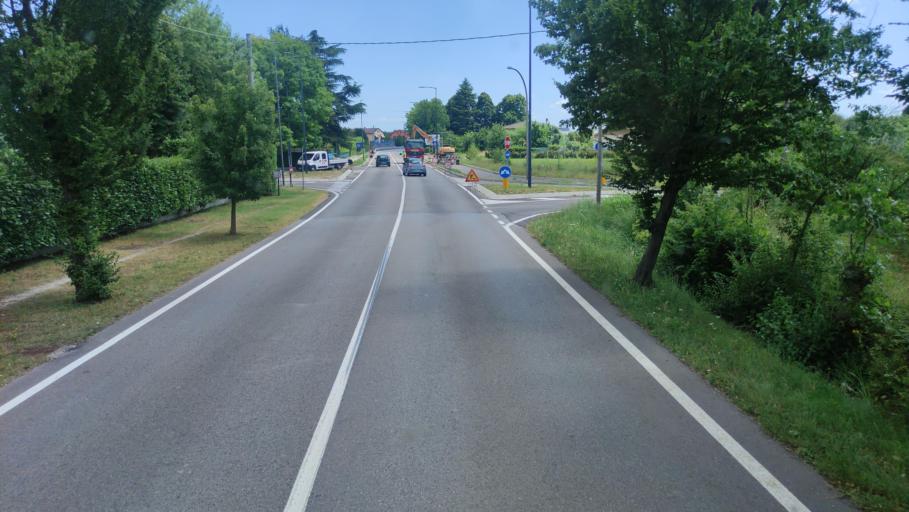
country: IT
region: Veneto
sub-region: Provincia di Venezia
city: Scorze
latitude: 45.5706
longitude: 12.1004
